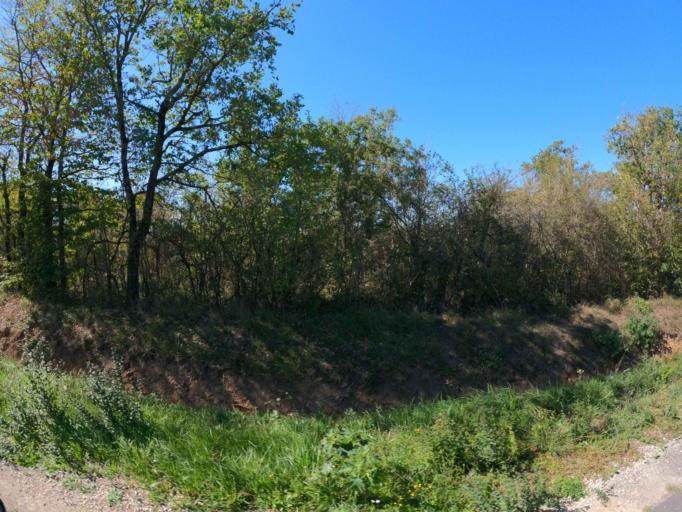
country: FR
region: Poitou-Charentes
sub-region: Departement de la Vienne
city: Lathus-Saint-Remy
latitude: 46.3598
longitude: 0.9430
